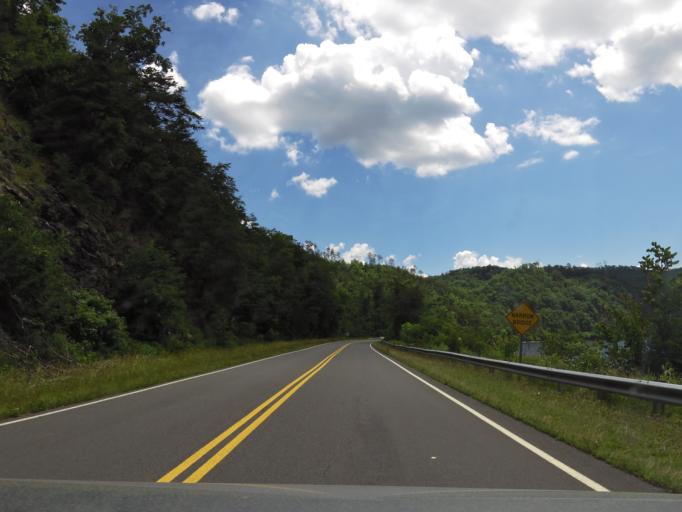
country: US
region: Tennessee
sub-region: Loudon County
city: Greenback
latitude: 35.5558
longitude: -84.0014
